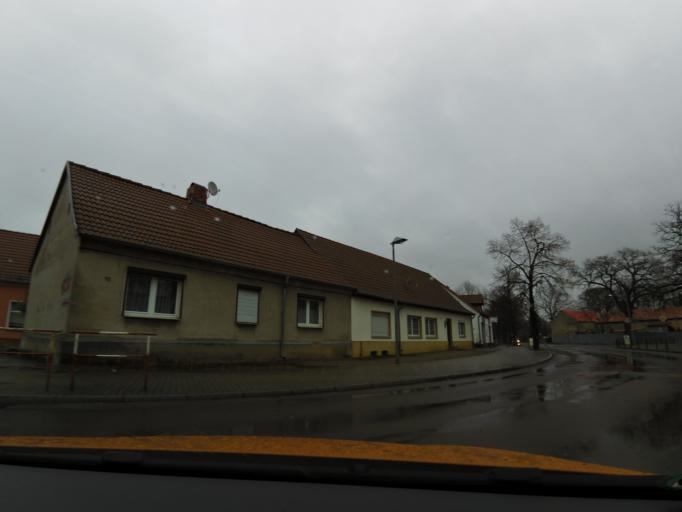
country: DE
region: Brandenburg
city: Zossen
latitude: 52.2400
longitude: 13.4327
